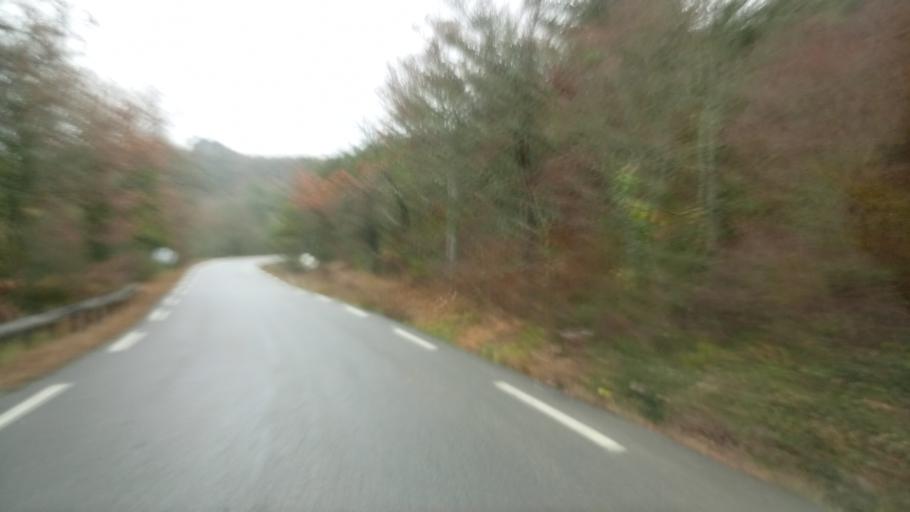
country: FR
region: Provence-Alpes-Cote d'Azur
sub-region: Departement du Var
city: Ginasservis
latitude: 43.7027
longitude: 5.8737
